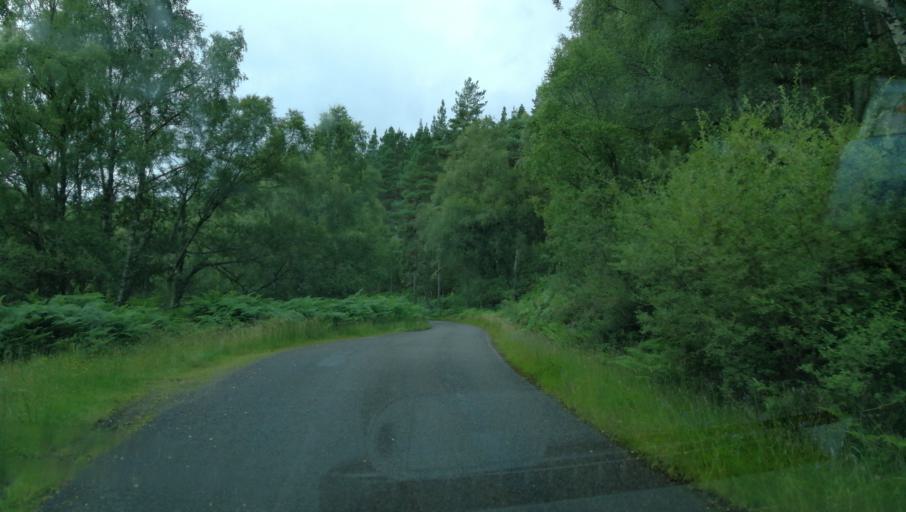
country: GB
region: Scotland
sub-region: Highland
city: Spean Bridge
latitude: 57.3010
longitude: -4.8946
